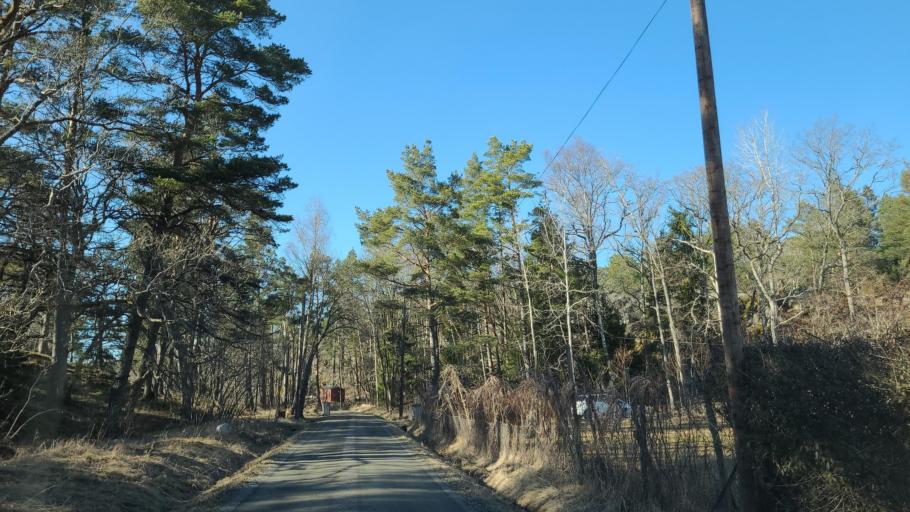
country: SE
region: Stockholm
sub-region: Varmdo Kommun
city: Holo
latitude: 59.3610
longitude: 18.6661
